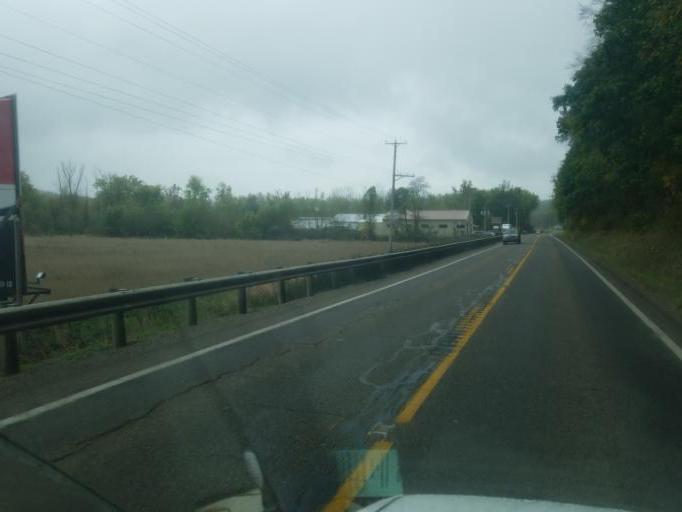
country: US
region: Ohio
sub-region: Holmes County
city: Millersburg
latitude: 40.5876
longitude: -81.9152
